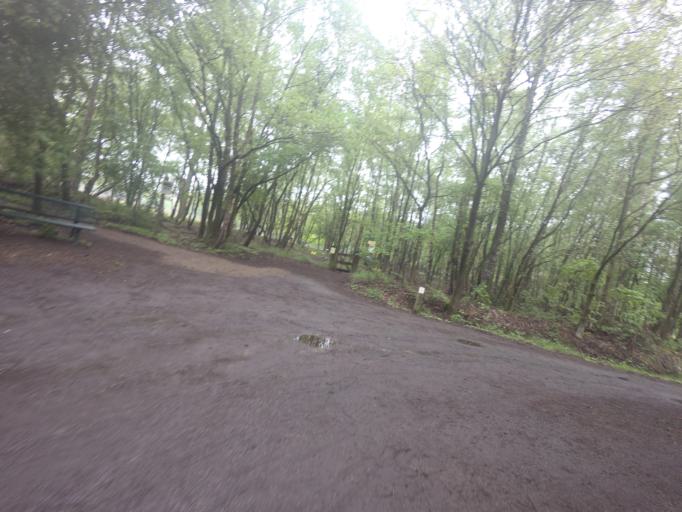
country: NL
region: Overijssel
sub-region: Gemeente Enschede
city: Enschede
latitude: 52.1418
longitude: 6.8662
